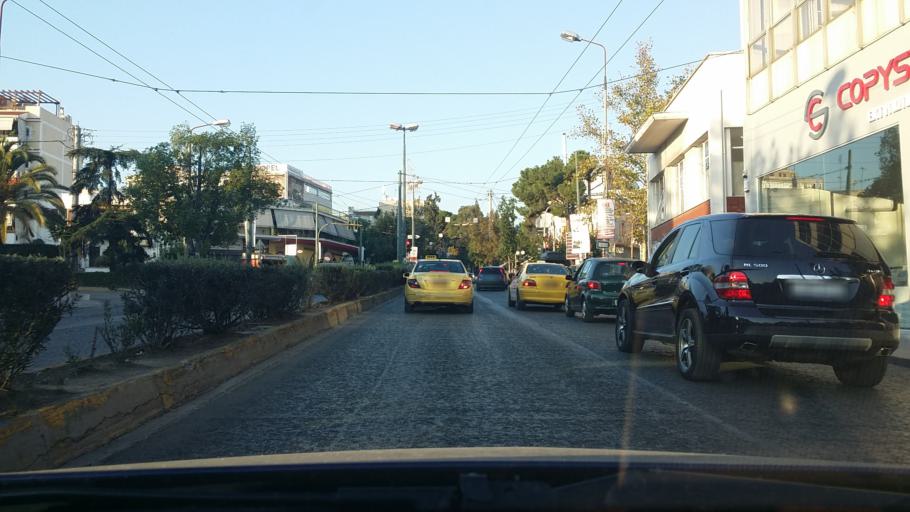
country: GR
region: Attica
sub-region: Nomarchia Athinas
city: Nea Chalkidona
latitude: 38.0268
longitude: 23.7320
